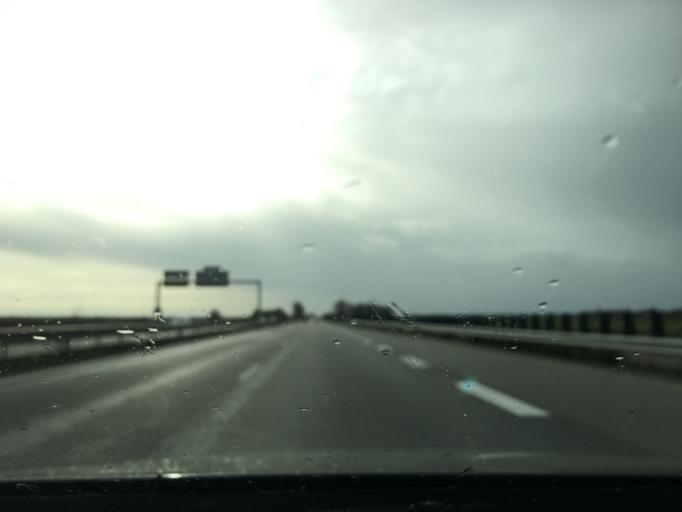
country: FR
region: Alsace
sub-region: Departement du Haut-Rhin
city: Meyenheim
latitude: 47.9492
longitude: 7.3648
